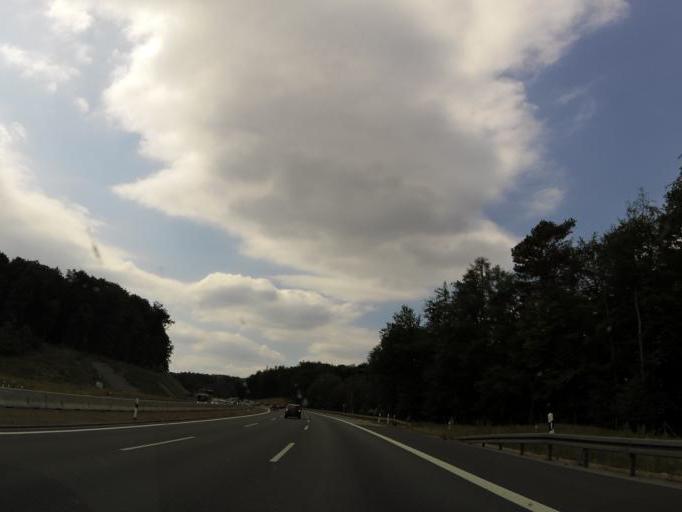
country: DE
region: Bavaria
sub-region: Regierungsbezirk Unterfranken
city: Waldbrunn
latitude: 49.7686
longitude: 9.7719
